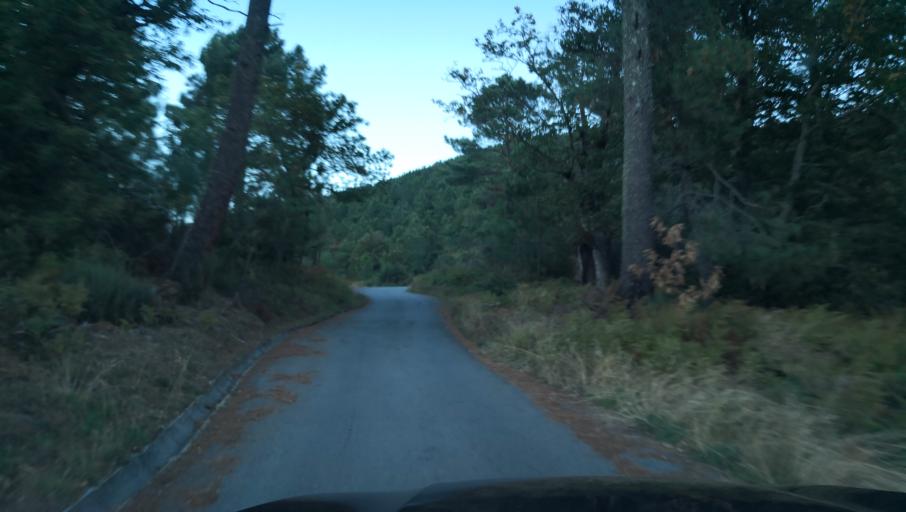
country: PT
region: Vila Real
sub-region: Santa Marta de Penaguiao
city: Santa Marta de Penaguiao
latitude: 41.2691
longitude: -7.8289
